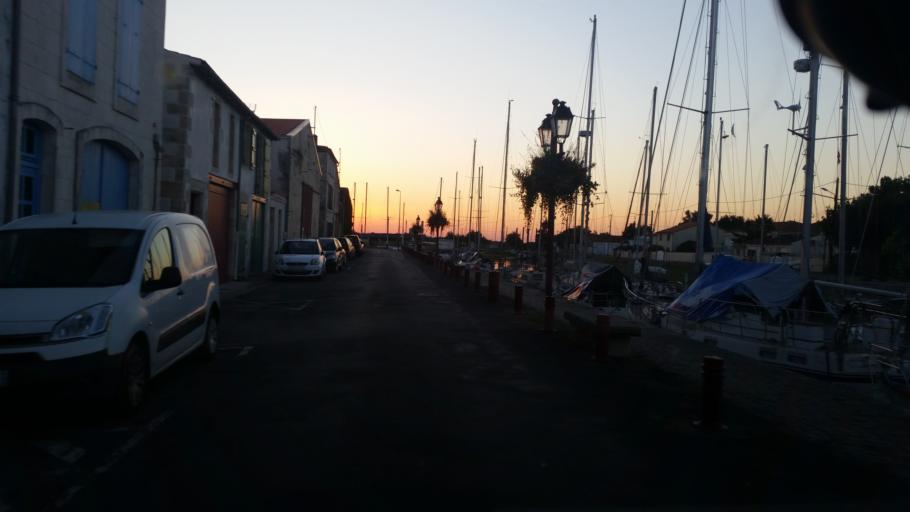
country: FR
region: Poitou-Charentes
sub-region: Departement de la Charente-Maritime
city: Marans
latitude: 46.3122
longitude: -0.9956
